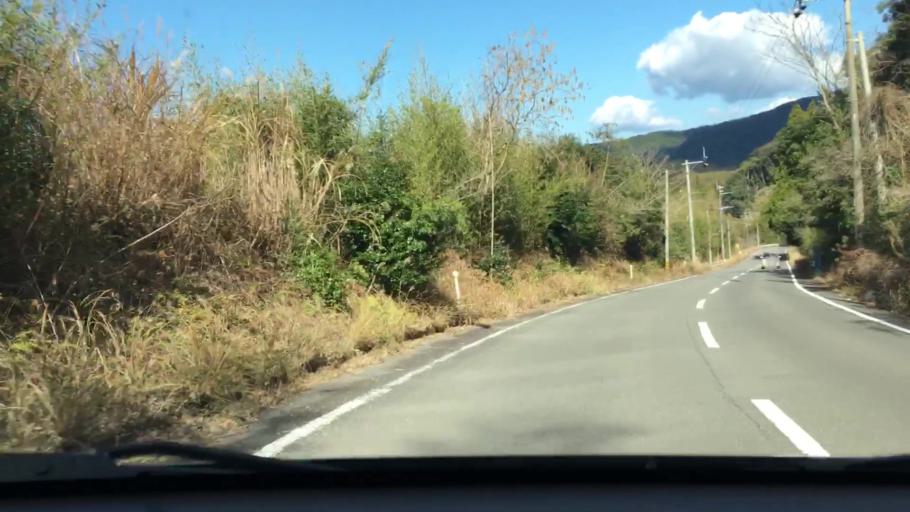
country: JP
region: Kagoshima
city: Ijuin
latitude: 31.7232
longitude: 130.4163
